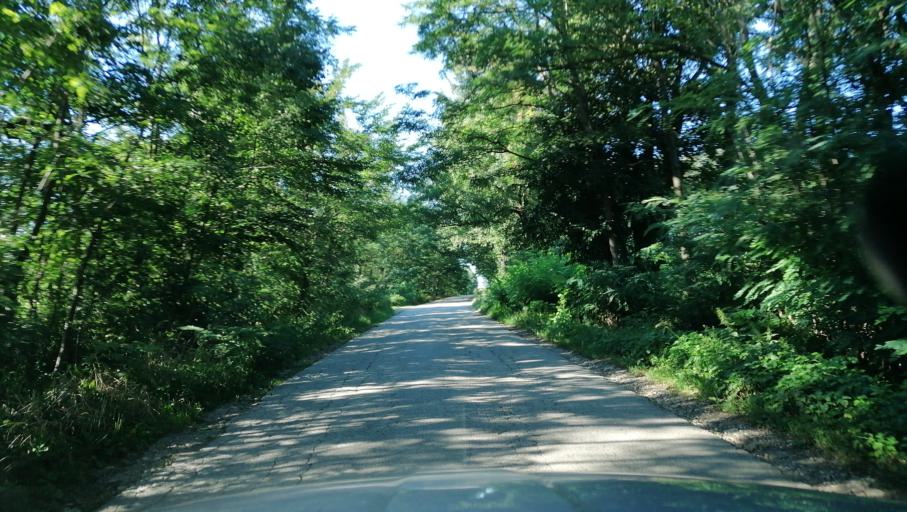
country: RS
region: Central Serbia
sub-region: Sumadijski Okrug
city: Knic
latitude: 43.8886
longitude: 20.6156
